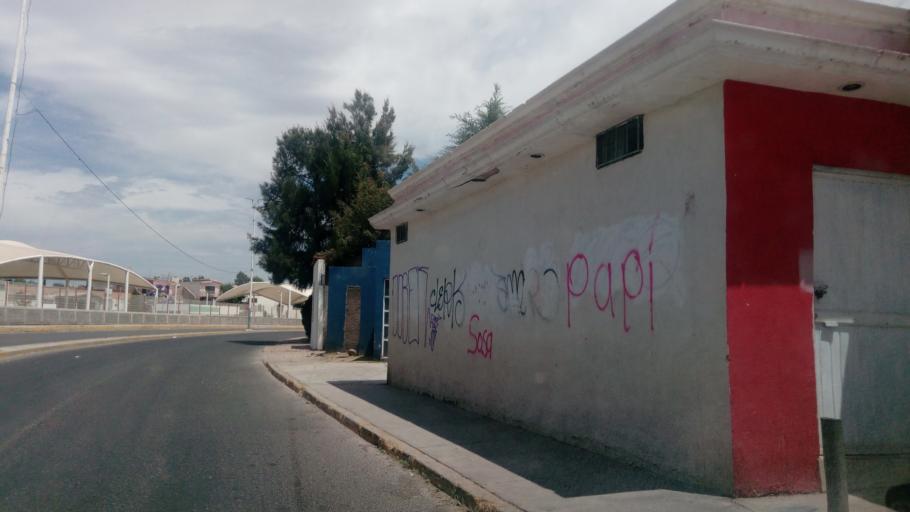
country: MX
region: Durango
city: Victoria de Durango
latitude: 24.0394
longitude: -104.6819
